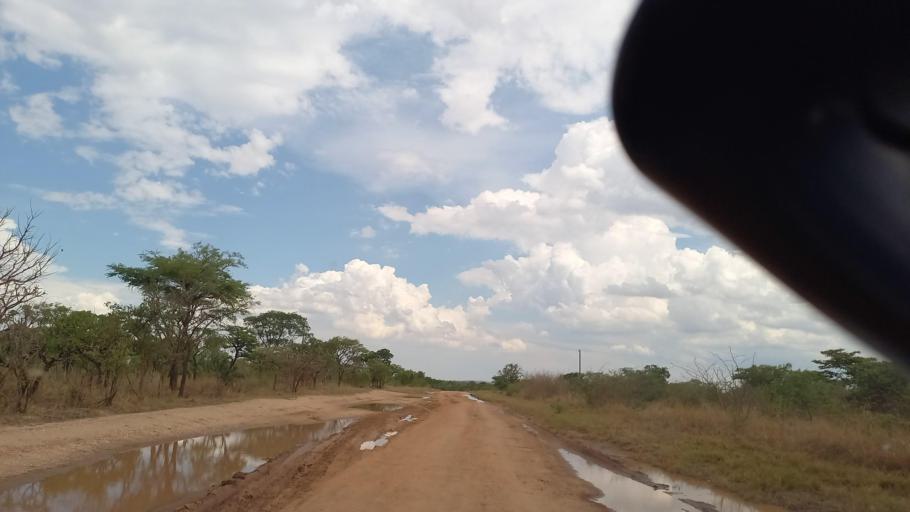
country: ZM
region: Southern
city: Nakambala
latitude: -16.0604
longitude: 27.9919
